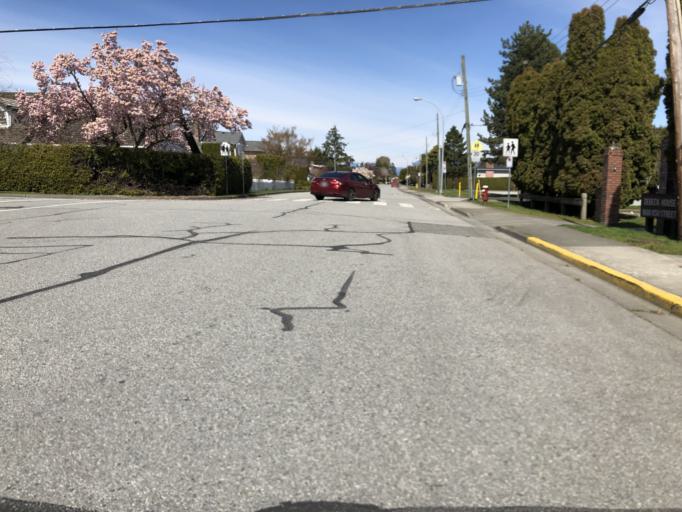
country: CA
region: British Columbia
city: Richmond
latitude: 49.1499
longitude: -123.1198
